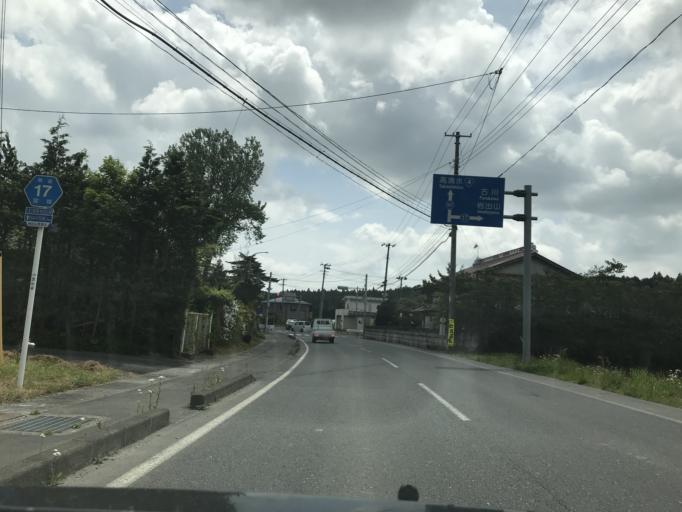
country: JP
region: Miyagi
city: Furukawa
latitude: 38.6932
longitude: 140.9312
